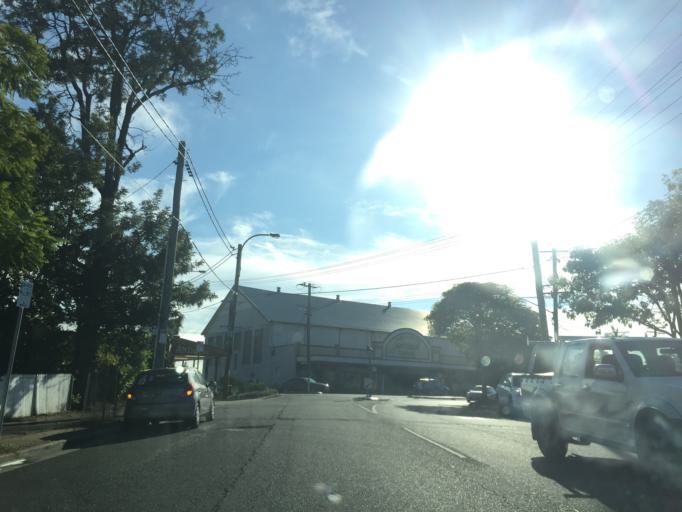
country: AU
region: Queensland
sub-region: Brisbane
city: Milton
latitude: -27.4587
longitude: 152.9941
